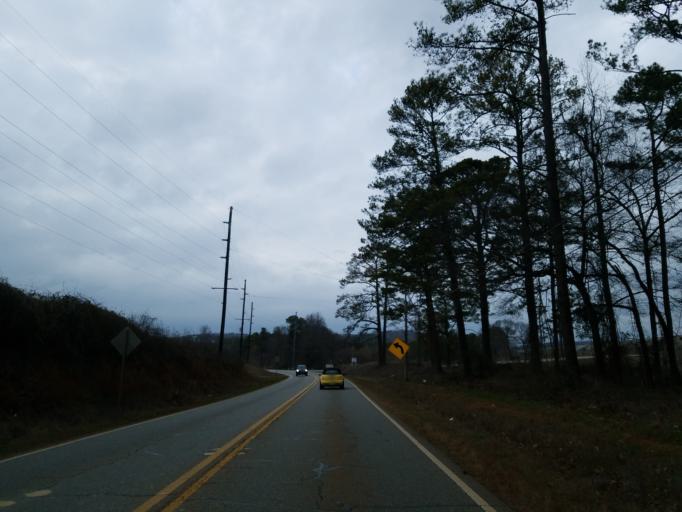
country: US
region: Georgia
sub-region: Bartow County
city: Emerson
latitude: 34.1415
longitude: -84.7651
